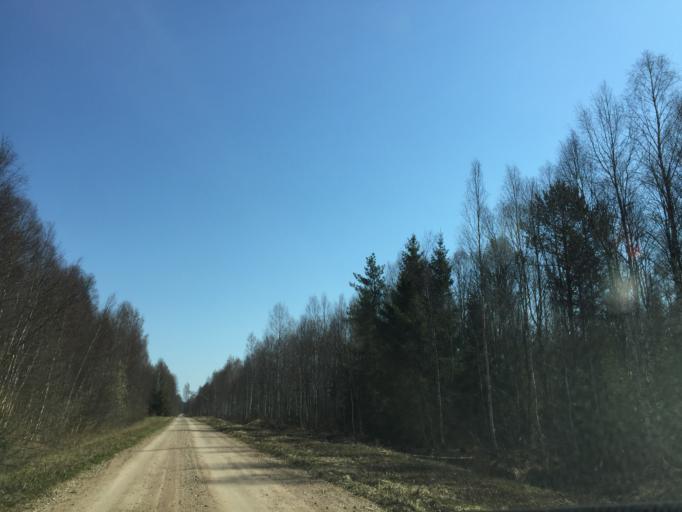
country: EE
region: Tartu
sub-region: Tartu linn
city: Tartu
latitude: 58.5290
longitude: 26.9159
